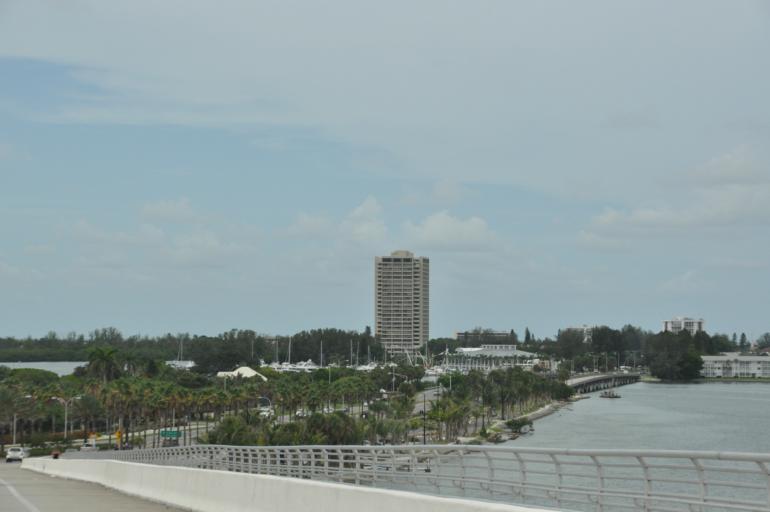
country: US
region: Florida
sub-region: Sarasota County
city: Sarasota
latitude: 27.3300
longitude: -82.5582
